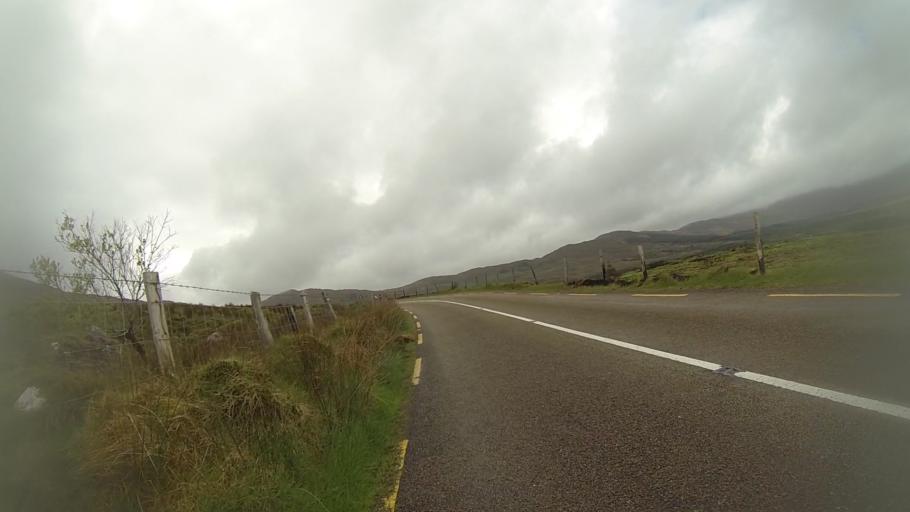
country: IE
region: Munster
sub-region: Ciarrai
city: Kenmare
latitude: 51.8815
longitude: -9.7943
